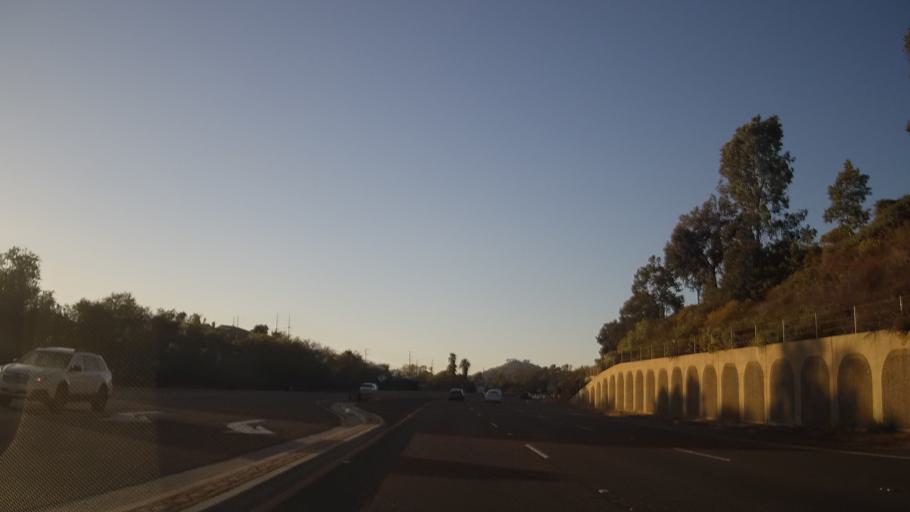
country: US
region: California
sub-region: San Diego County
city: Rancho San Diego
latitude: 32.7390
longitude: -116.9539
